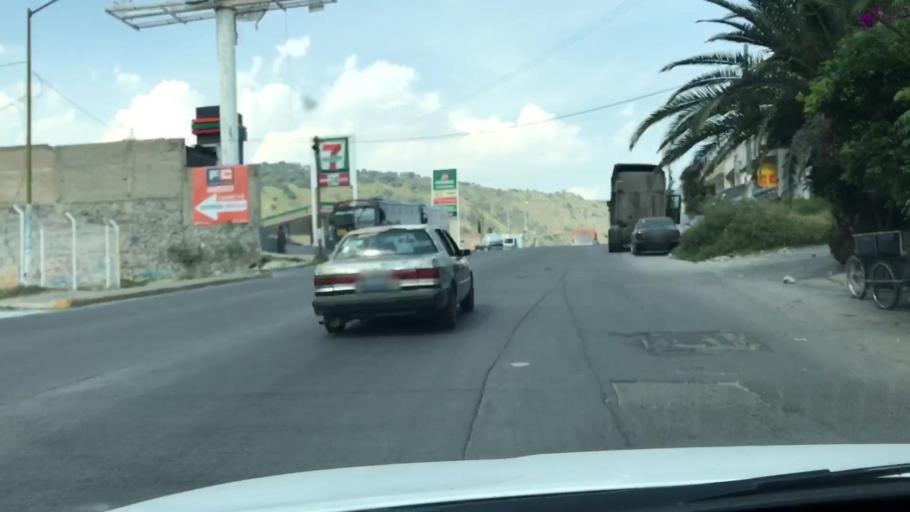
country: MX
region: Jalisco
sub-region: Tlajomulco de Zuniga
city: Palomar
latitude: 20.6408
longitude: -103.4613
